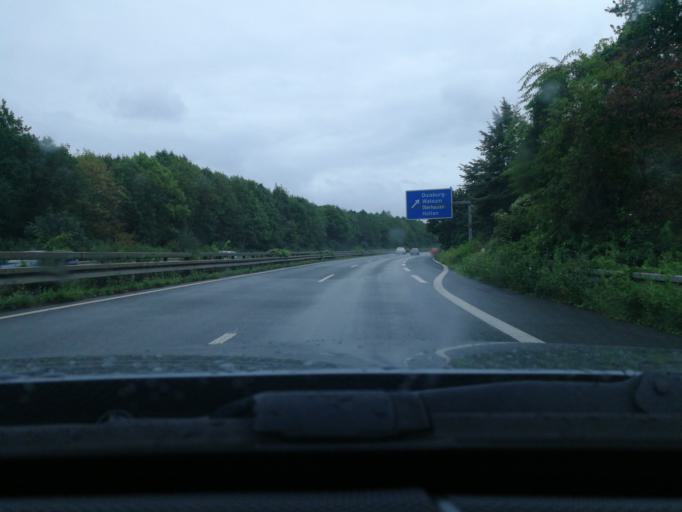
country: DE
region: North Rhine-Westphalia
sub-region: Regierungsbezirk Dusseldorf
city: Dinslaken
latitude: 51.5319
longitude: 6.7573
